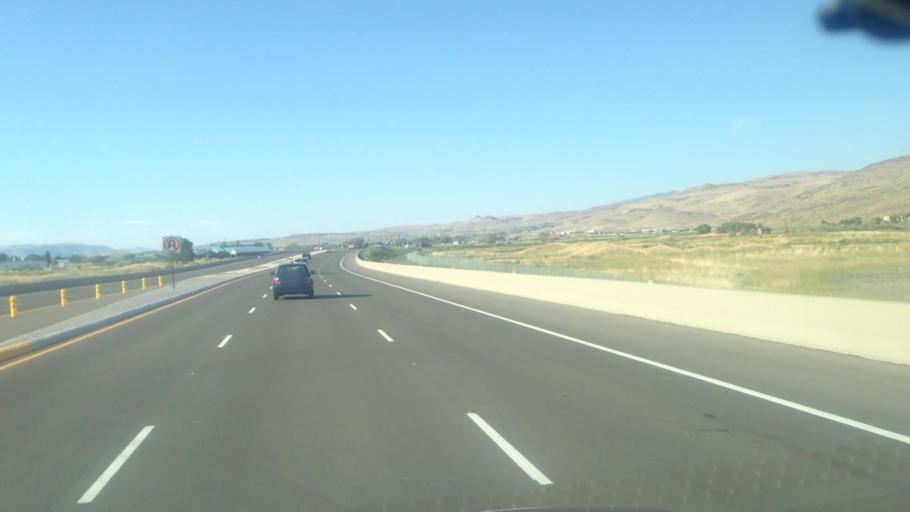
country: US
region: Nevada
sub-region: Washoe County
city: Sparks
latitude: 39.4930
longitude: -119.7319
